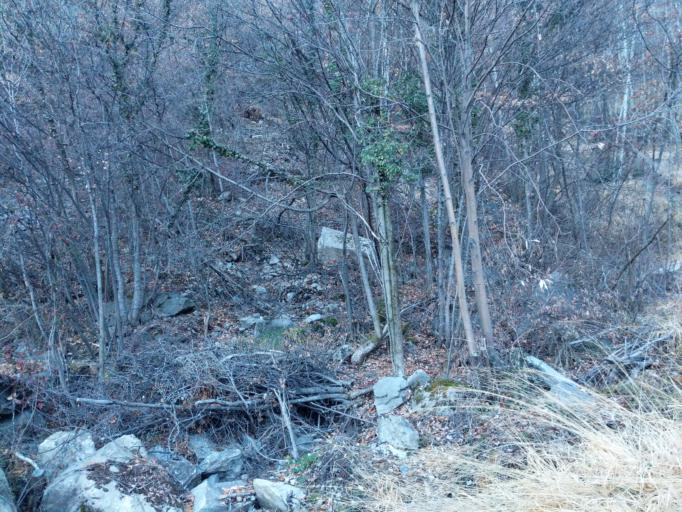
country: FR
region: Rhone-Alpes
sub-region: Departement de la Savoie
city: Villargondran
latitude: 45.2575
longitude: 6.4166
